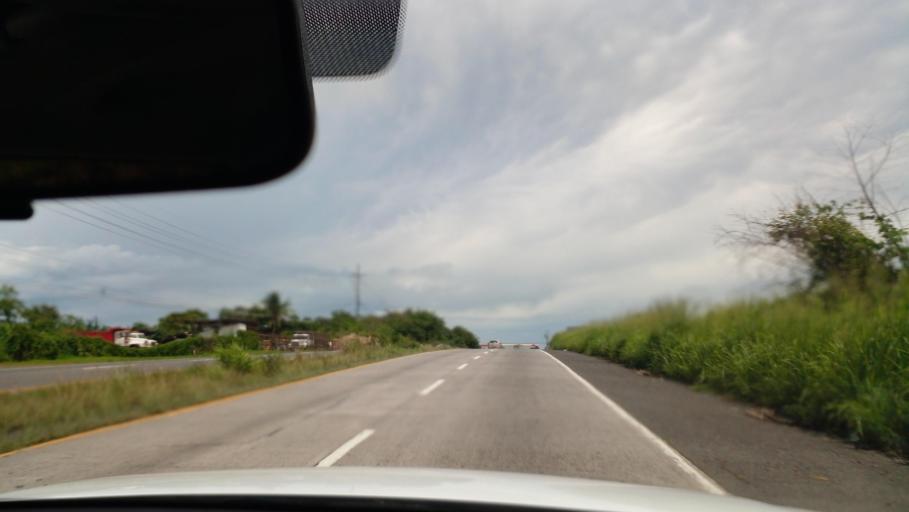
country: PA
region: Panama
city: Nueva Gorgona
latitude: 8.4901
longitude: -79.9582
